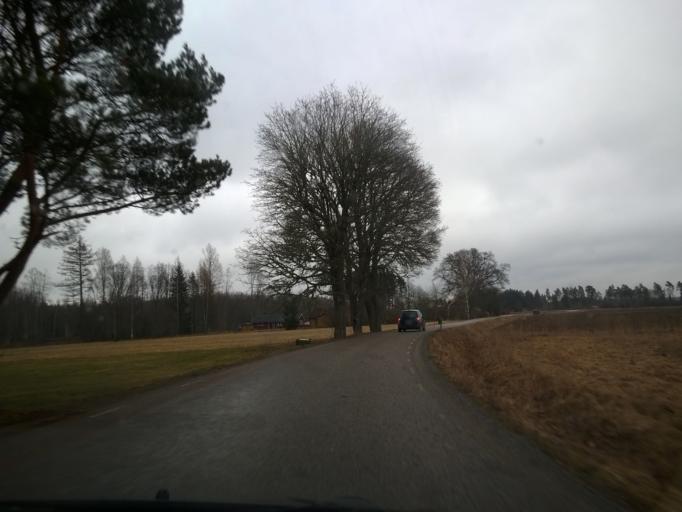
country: SE
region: Uppsala
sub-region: Osthammars Kommun
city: Bjorklinge
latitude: 60.1633
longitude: 17.5257
